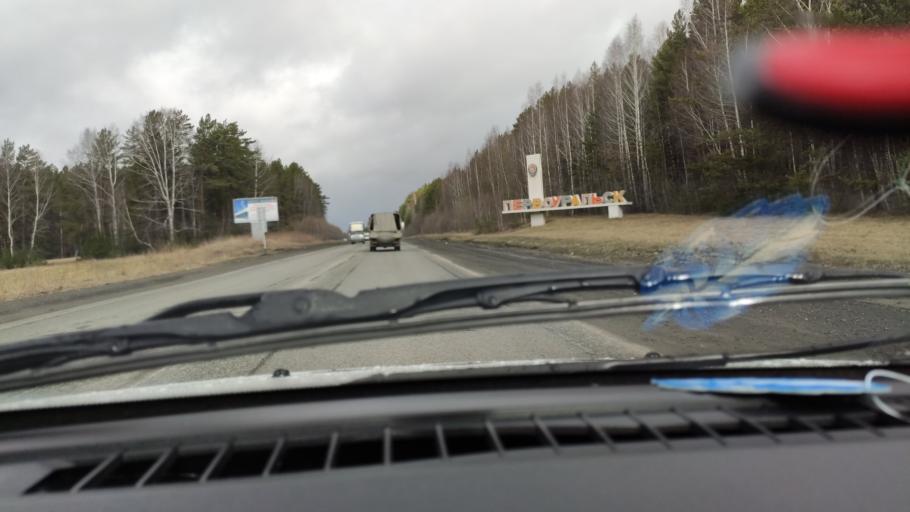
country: RU
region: Sverdlovsk
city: Talitsa
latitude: 56.8721
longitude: 60.0372
